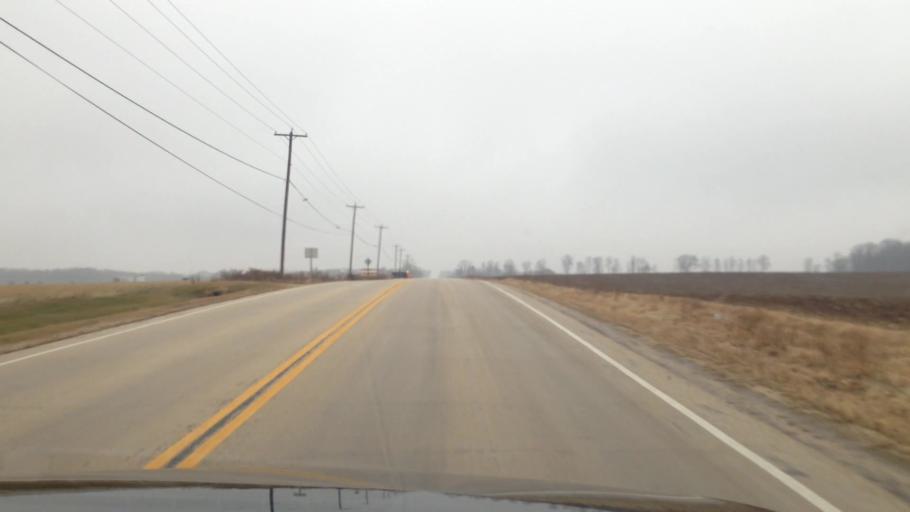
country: US
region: Wisconsin
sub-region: Washington County
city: Richfield
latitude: 43.2513
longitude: -88.1625
